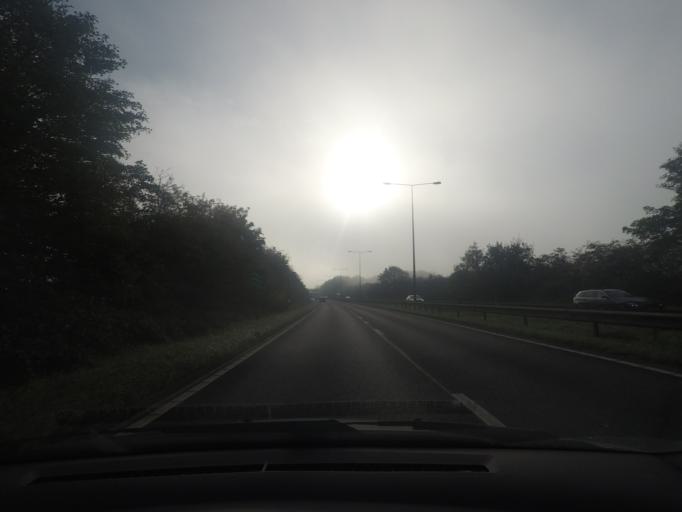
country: GB
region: England
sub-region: East Riding of Yorkshire
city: Welton
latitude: 53.7342
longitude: -0.5579
